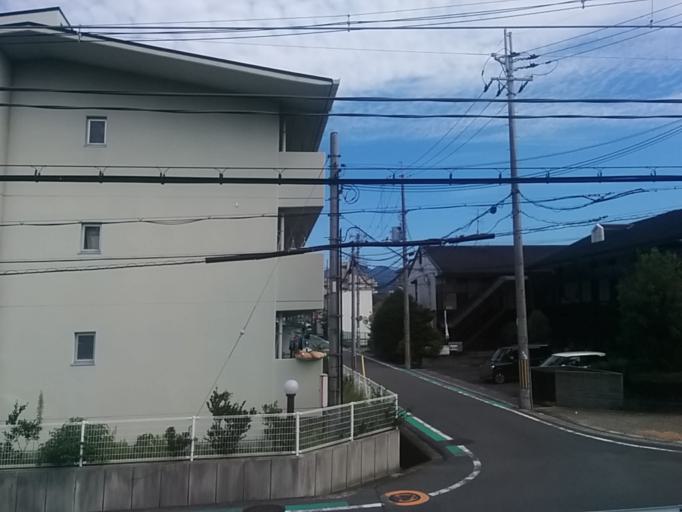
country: JP
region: Nara
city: Kashihara-shi
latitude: 34.4883
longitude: 135.7945
